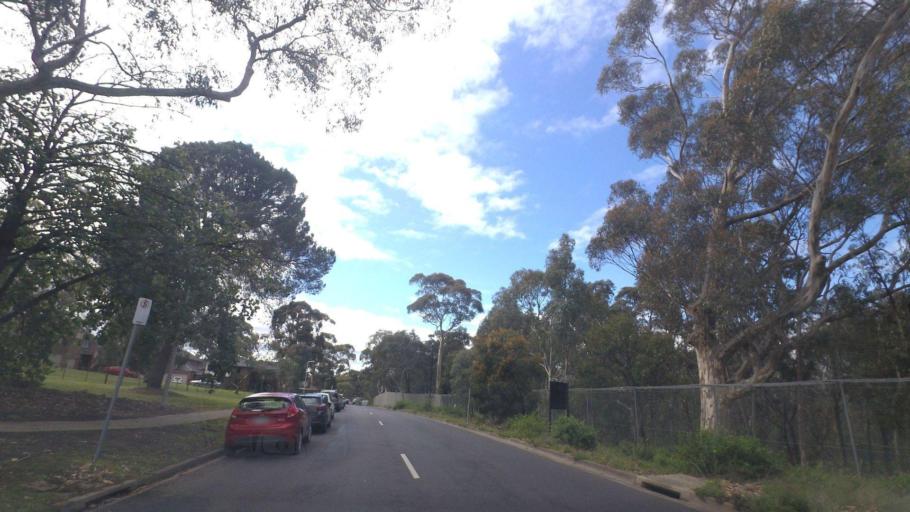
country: AU
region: Victoria
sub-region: Darebin
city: Kingsbury
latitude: -37.7156
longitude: 145.0512
